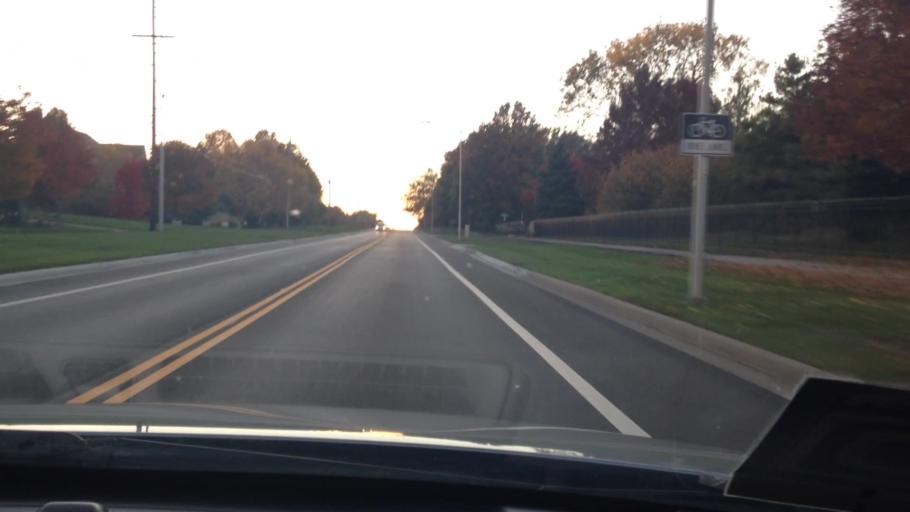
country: US
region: Kansas
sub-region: Johnson County
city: Olathe
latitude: 38.8691
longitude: -94.7487
